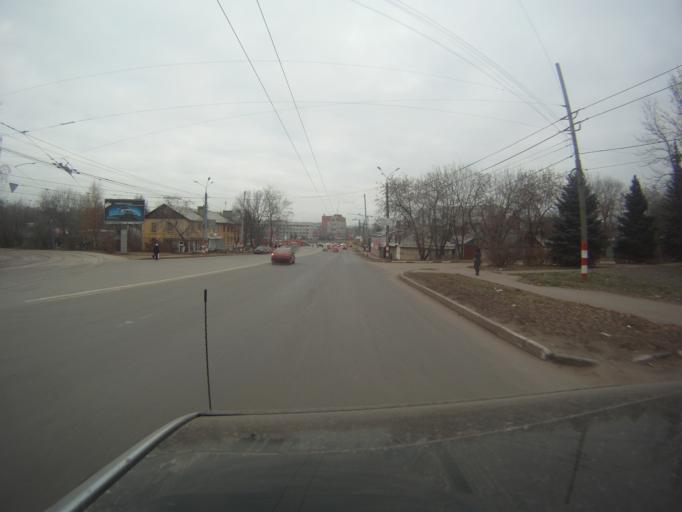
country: RU
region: Nizjnij Novgorod
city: Nizhniy Novgorod
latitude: 56.2958
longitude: 44.0315
